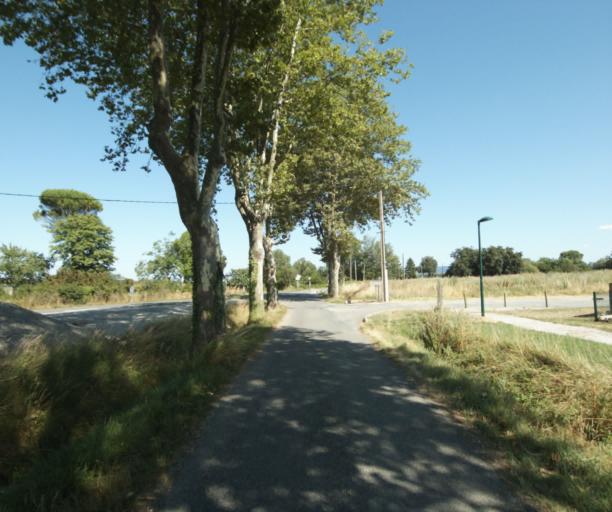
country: FR
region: Midi-Pyrenees
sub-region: Departement de la Haute-Garonne
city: Saint-Felix-Lauragais
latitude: 43.4894
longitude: 1.9046
